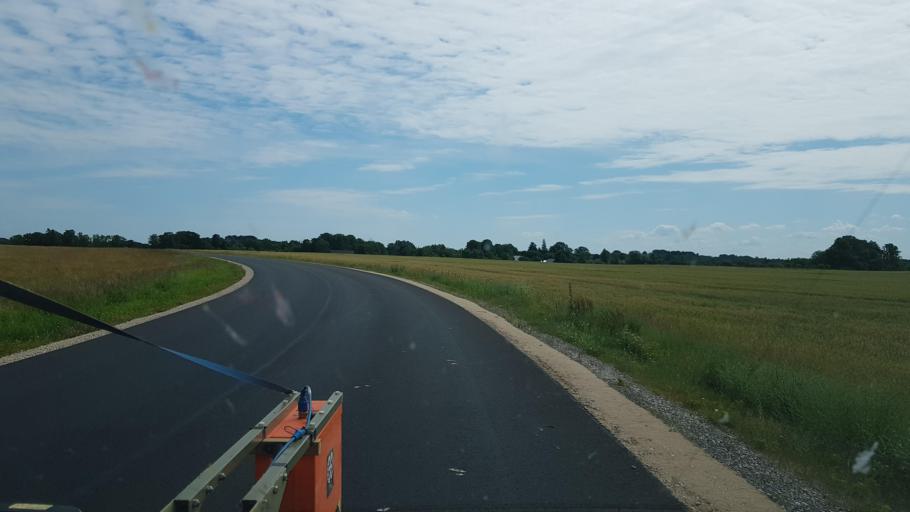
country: EE
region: Paernumaa
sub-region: Halinga vald
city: Parnu-Jaagupi
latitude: 58.6196
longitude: 24.3050
